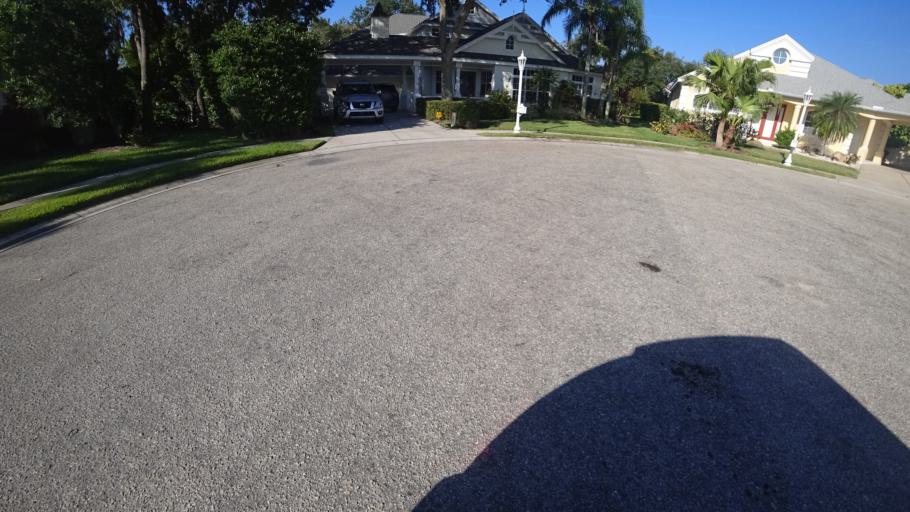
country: US
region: Florida
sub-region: Manatee County
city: Ellenton
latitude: 27.5049
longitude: -82.5051
